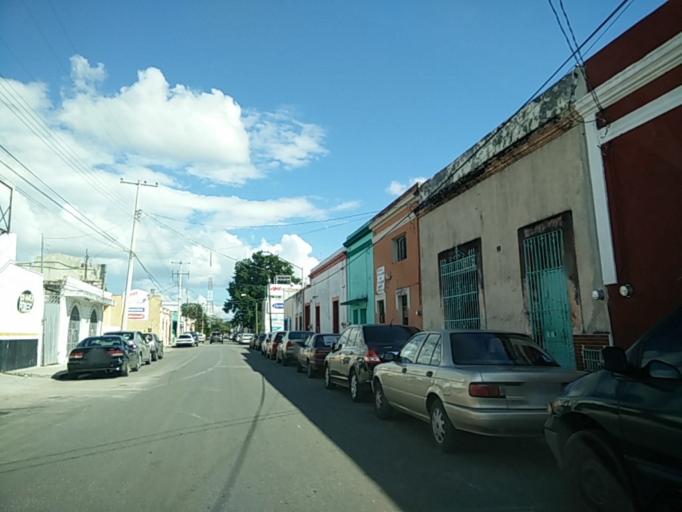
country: MX
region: Yucatan
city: Merida
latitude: 20.9772
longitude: -89.6169
